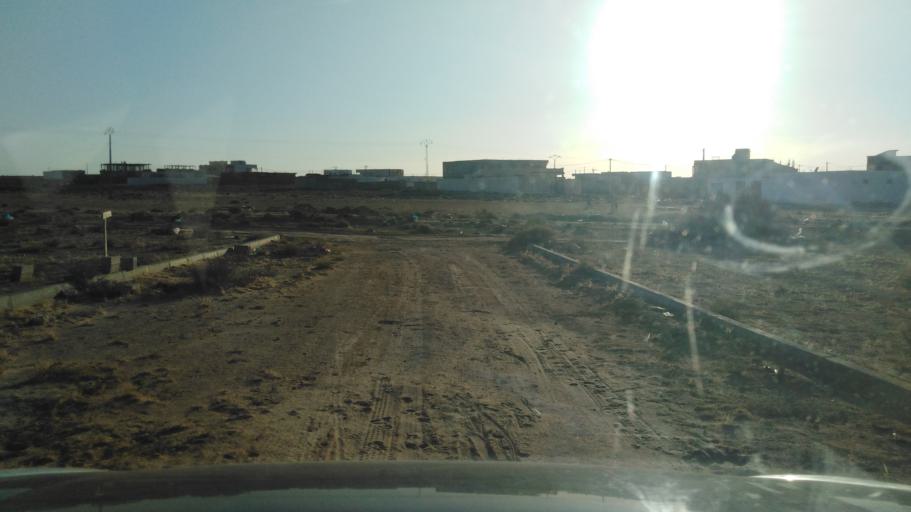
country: TN
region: Qabis
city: Gabes
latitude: 33.9504
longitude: 10.0153
